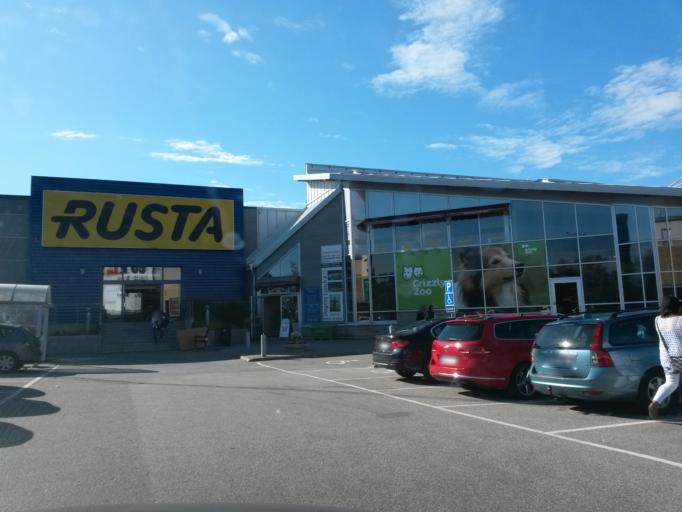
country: SE
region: Vaestra Goetaland
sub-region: Boras Kommun
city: Boras
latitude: 57.7320
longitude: 12.9334
